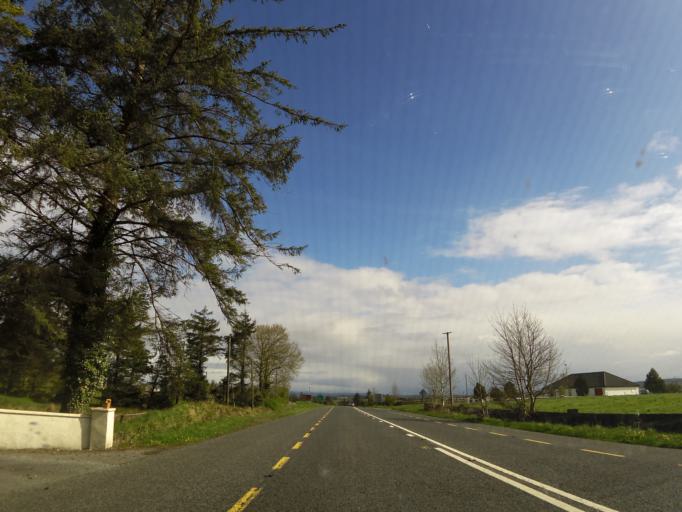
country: IE
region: Connaught
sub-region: Sligo
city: Tobercurry
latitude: 53.9166
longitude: -8.7899
